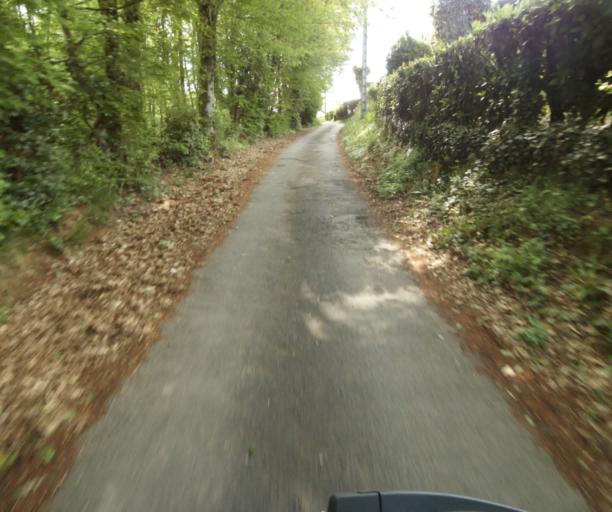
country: FR
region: Limousin
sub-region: Departement de la Correze
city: Tulle
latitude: 45.2661
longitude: 1.7809
